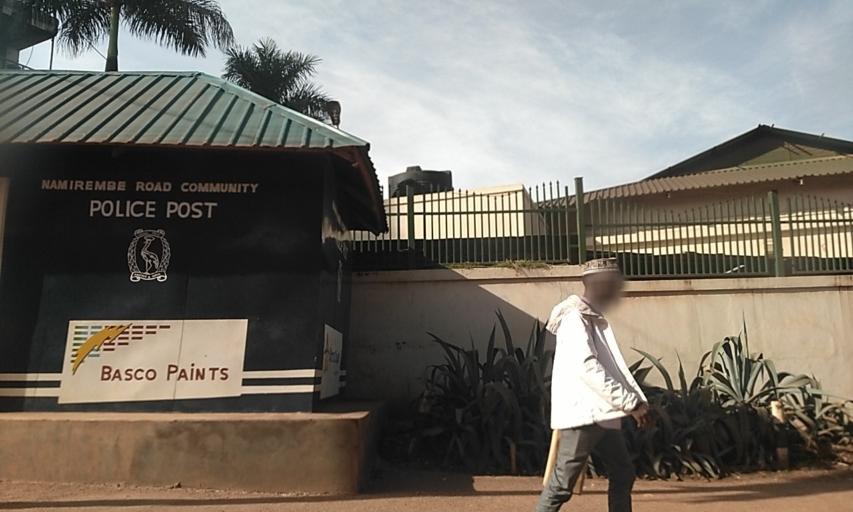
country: UG
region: Central Region
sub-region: Kampala District
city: Kampala
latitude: 0.3134
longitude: 32.5708
